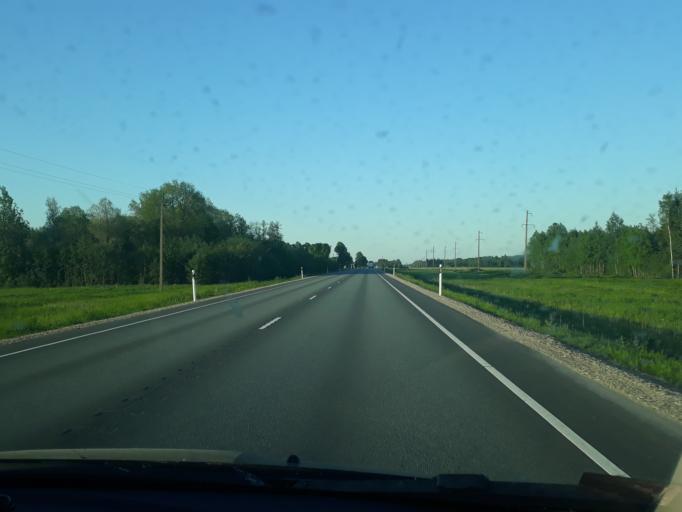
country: EE
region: Paernumaa
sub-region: Sindi linn
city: Sindi
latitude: 58.4794
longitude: 24.7323
